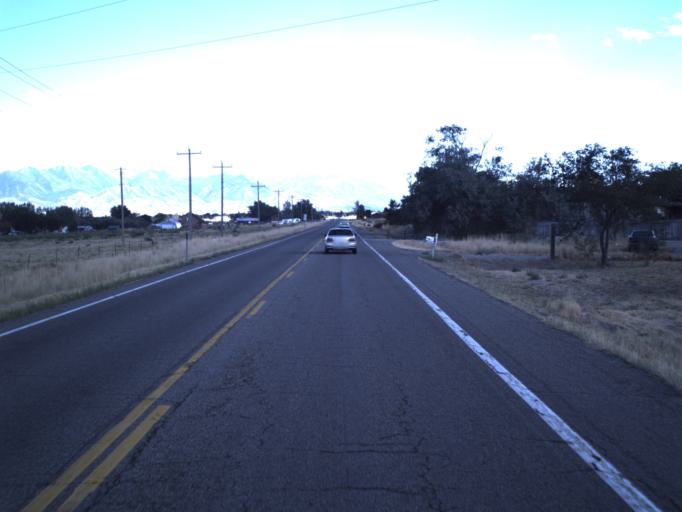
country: US
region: Utah
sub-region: Tooele County
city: Grantsville
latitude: 40.6160
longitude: -112.4985
